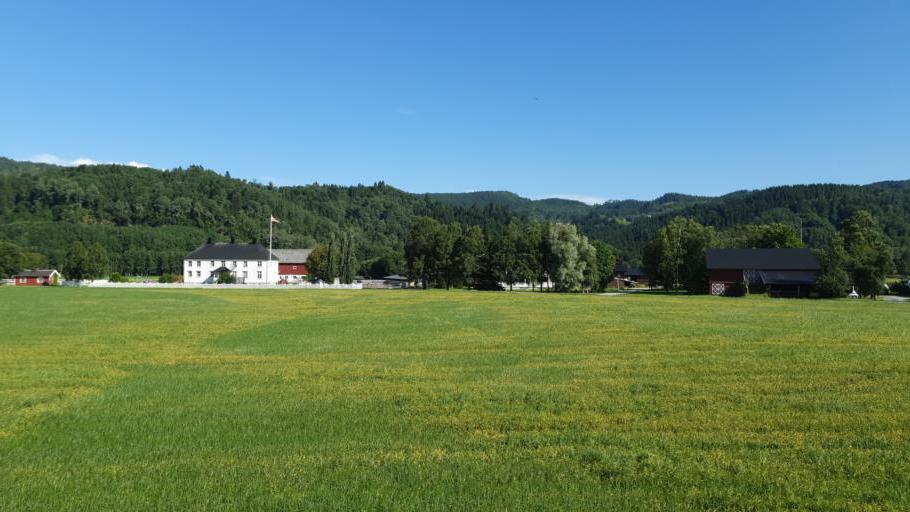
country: NO
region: Sor-Trondelag
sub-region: Orkdal
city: Orkanger
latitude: 63.2034
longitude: 9.7831
